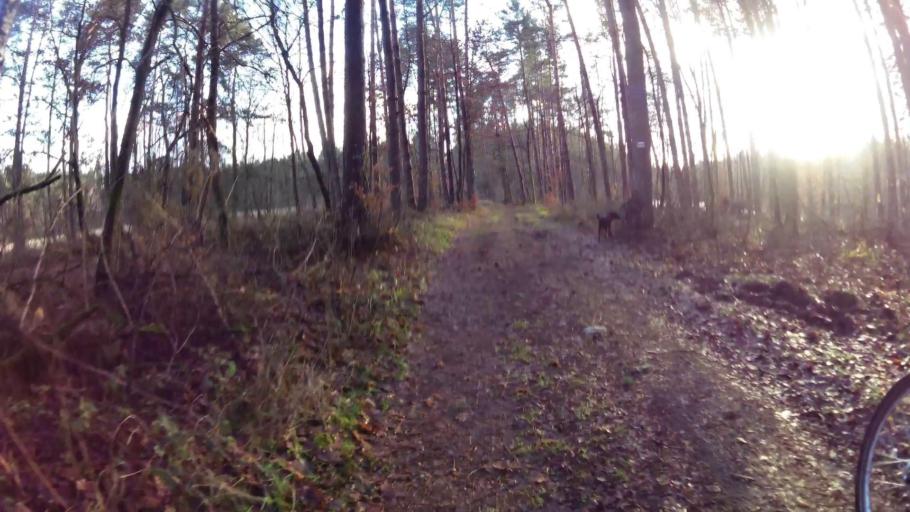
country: PL
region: West Pomeranian Voivodeship
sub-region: Powiat bialogardzki
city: Tychowo
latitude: 54.0612
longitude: 16.3036
